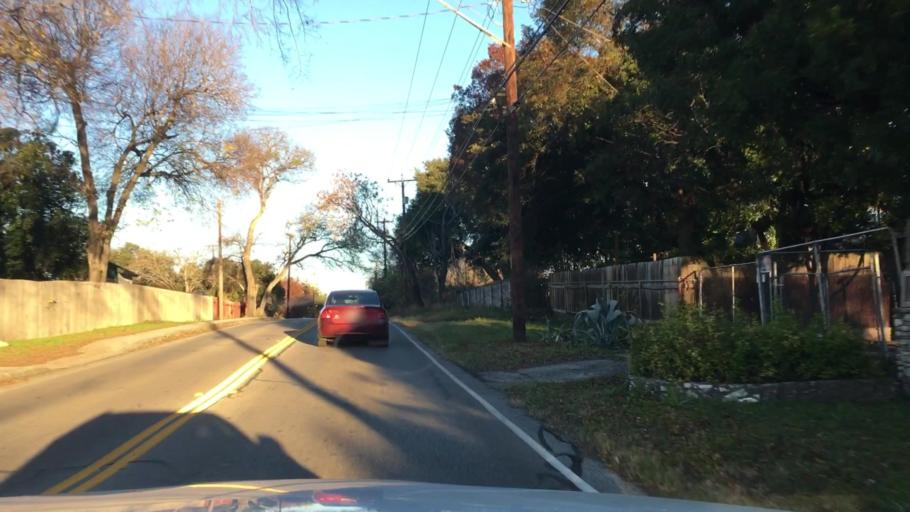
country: US
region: Texas
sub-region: Bexar County
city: Castle Hills
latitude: 29.5362
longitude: -98.5028
